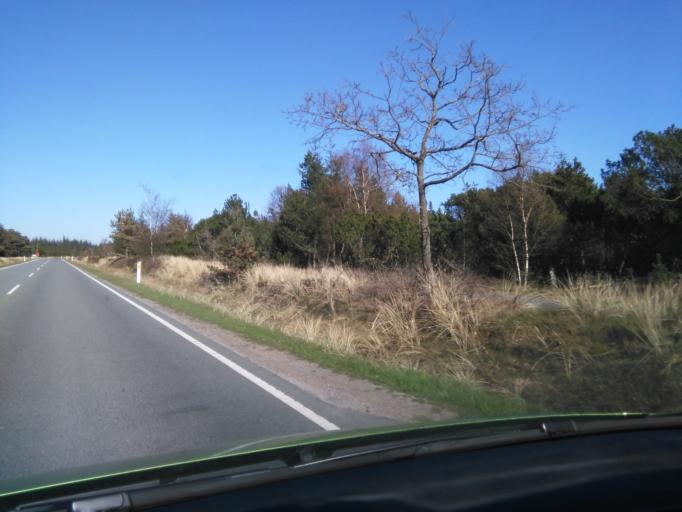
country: DK
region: South Denmark
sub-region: Varde Kommune
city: Oksbol
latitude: 55.5653
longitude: 8.1765
